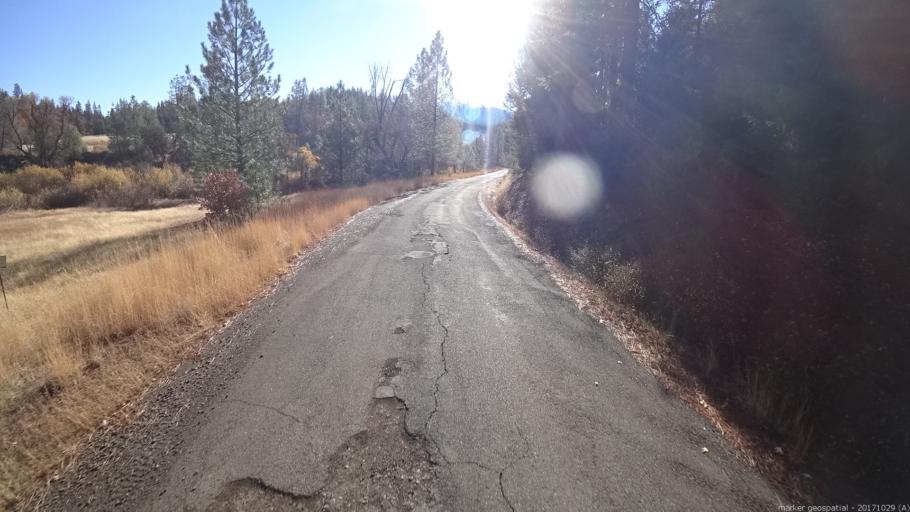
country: US
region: California
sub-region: Trinity County
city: Hayfork
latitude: 40.3615
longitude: -122.9655
